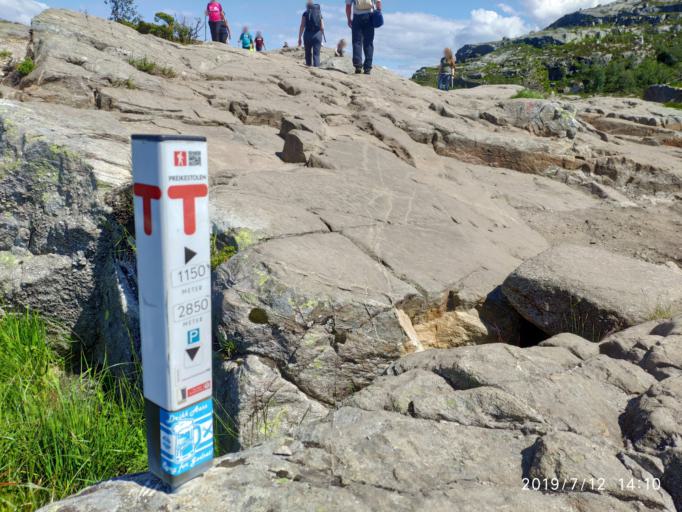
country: NO
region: Rogaland
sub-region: Forsand
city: Forsand
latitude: 58.9888
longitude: 6.1753
